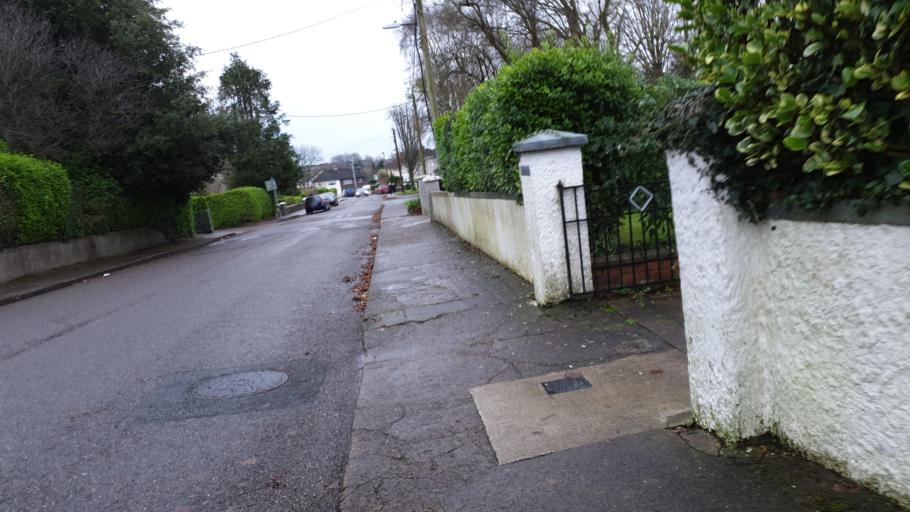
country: IE
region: Munster
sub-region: County Cork
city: Cork
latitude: 51.8897
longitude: -8.4238
